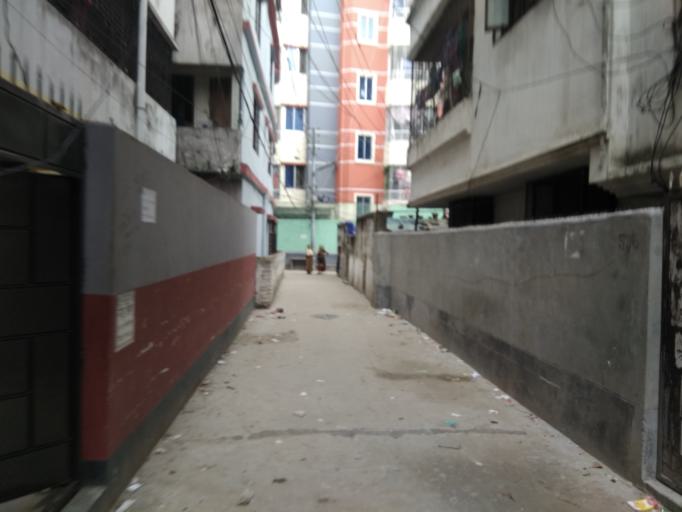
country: BD
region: Dhaka
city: Azimpur
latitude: 23.7973
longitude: 90.3775
